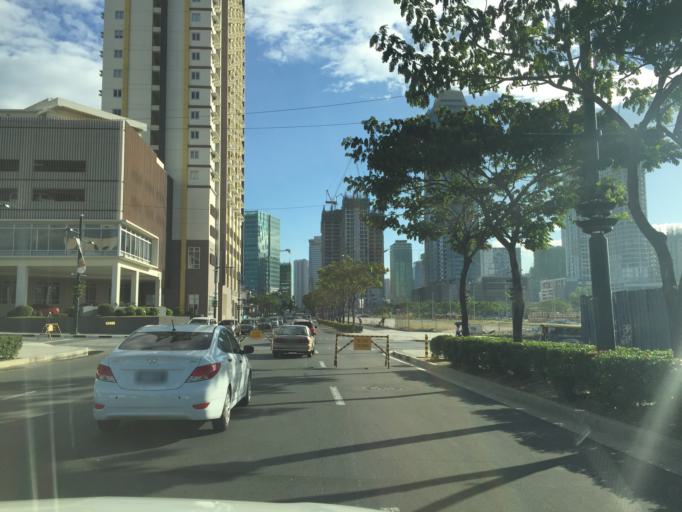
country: PH
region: Metro Manila
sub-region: Makati City
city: Makati City
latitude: 14.5611
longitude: 121.0549
